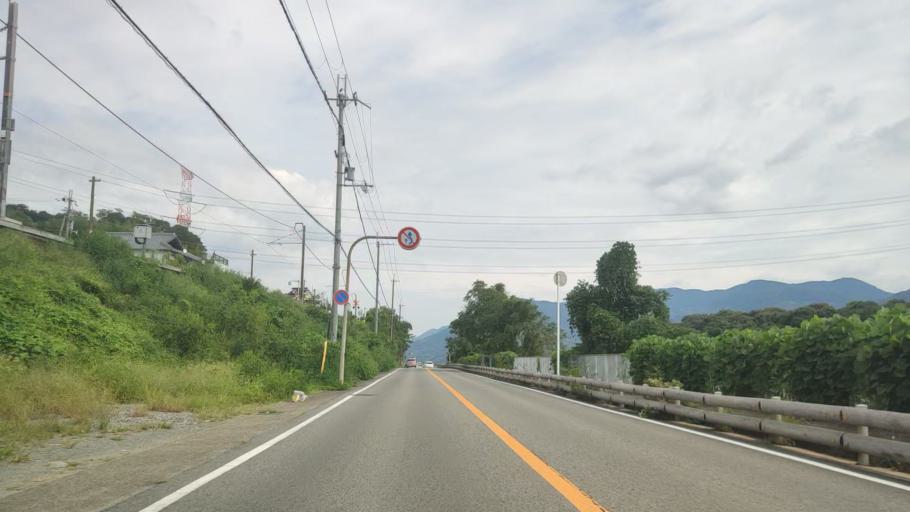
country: JP
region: Wakayama
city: Iwade
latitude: 34.2798
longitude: 135.4512
